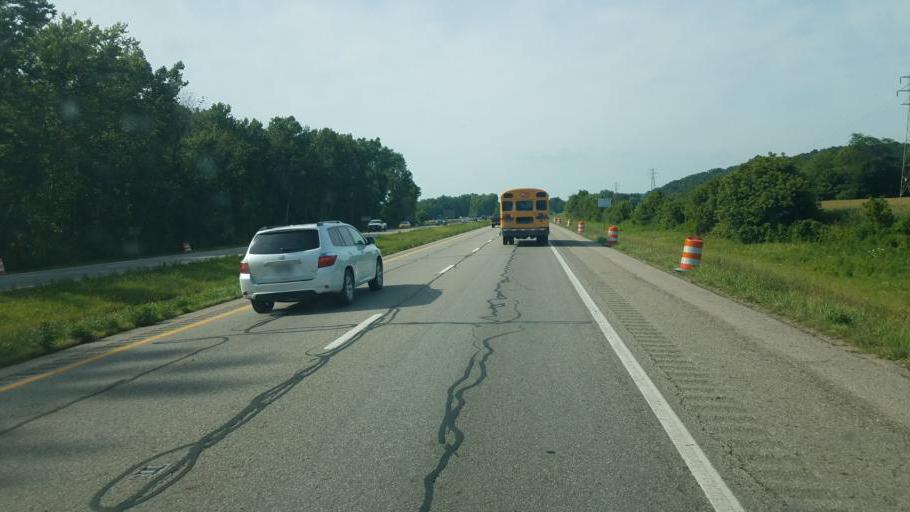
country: US
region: Ohio
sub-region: Fairfield County
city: Lancaster
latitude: 39.6270
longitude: -82.5517
